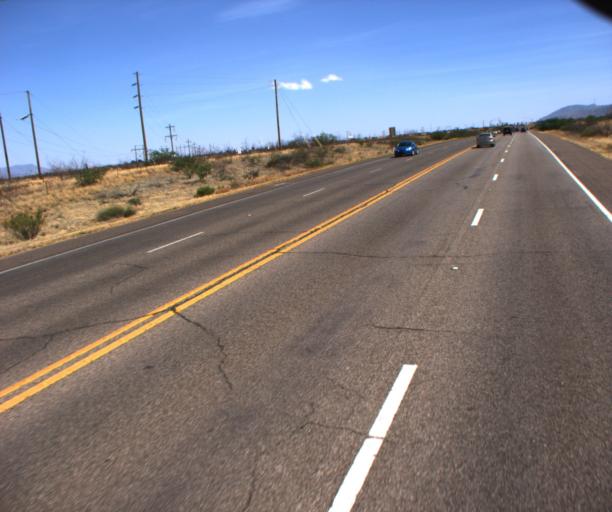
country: US
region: Arizona
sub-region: Cochise County
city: Sierra Vista
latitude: 31.5784
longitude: -110.3173
